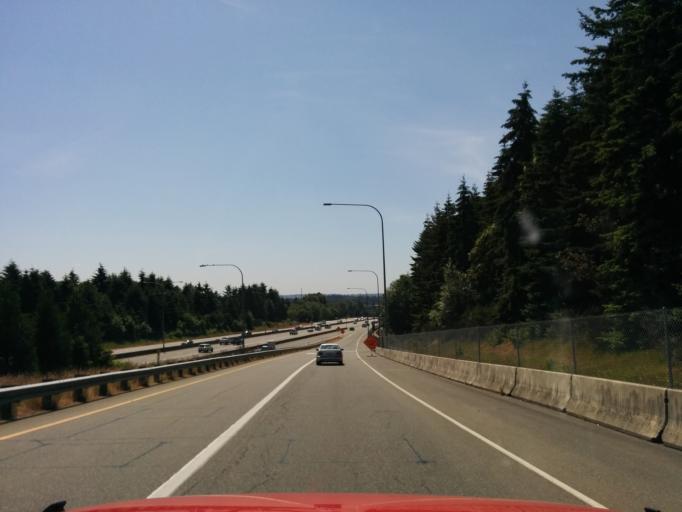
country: US
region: Washington
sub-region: King County
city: Redmond
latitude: 47.6349
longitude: -122.1437
